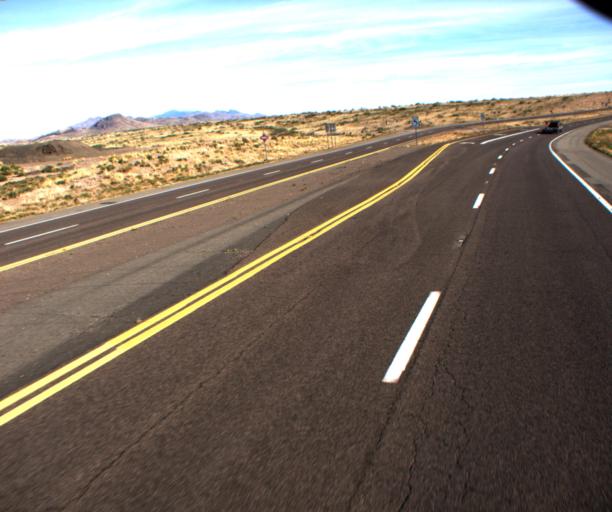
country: US
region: Arizona
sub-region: Cochise County
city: Willcox
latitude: 32.3615
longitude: -109.6813
